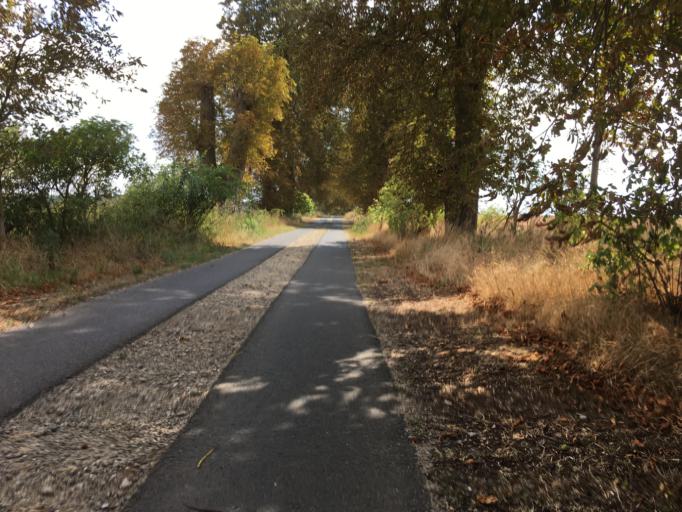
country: DE
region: Brandenburg
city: Zehdenick
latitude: 53.0819
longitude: 13.2859
